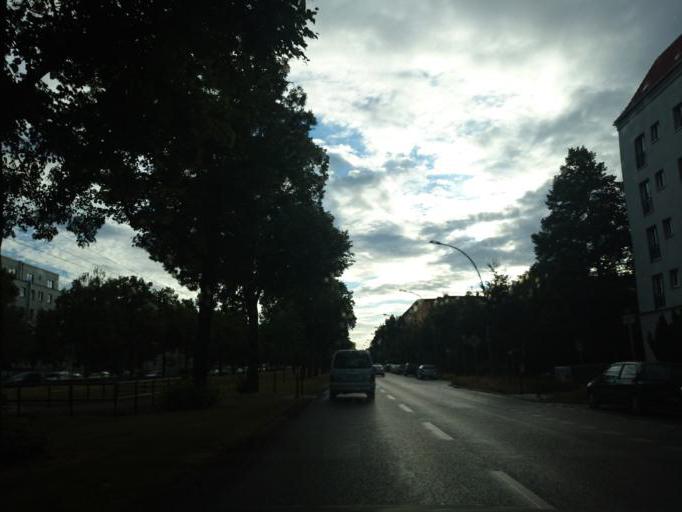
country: DE
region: Berlin
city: Prenzlauer Berg Bezirk
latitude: 52.5530
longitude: 13.4229
